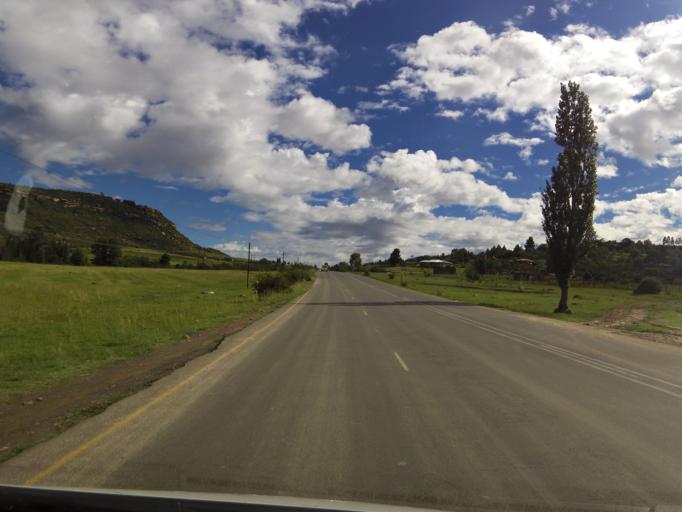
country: LS
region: Maseru
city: Maseru
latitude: -29.2554
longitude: 27.6030
